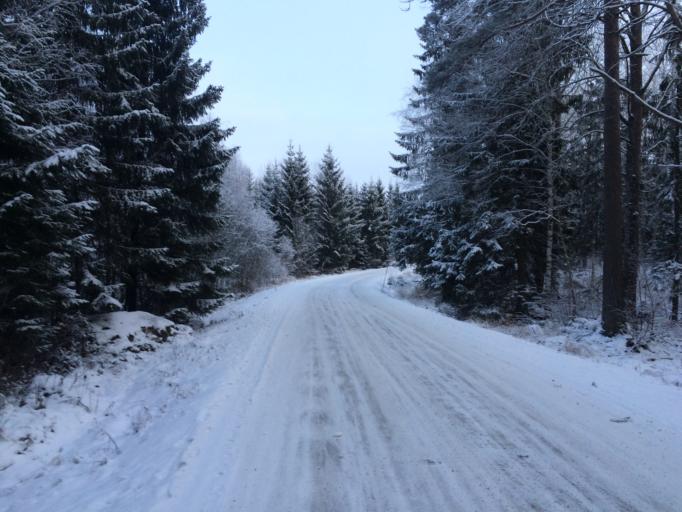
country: SE
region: Uppsala
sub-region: Enkopings Kommun
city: Orsundsbro
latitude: 59.9088
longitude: 17.1961
